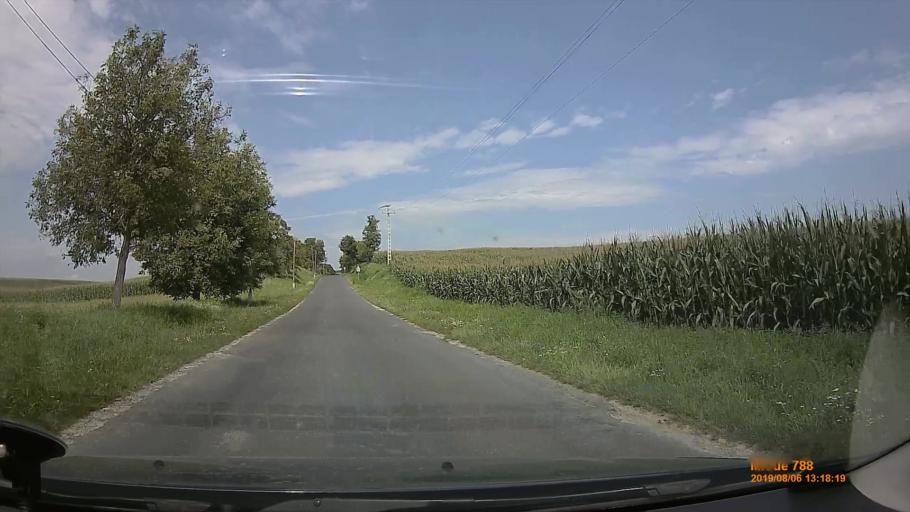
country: HU
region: Zala
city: Pacsa
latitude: 46.6323
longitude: 17.0610
